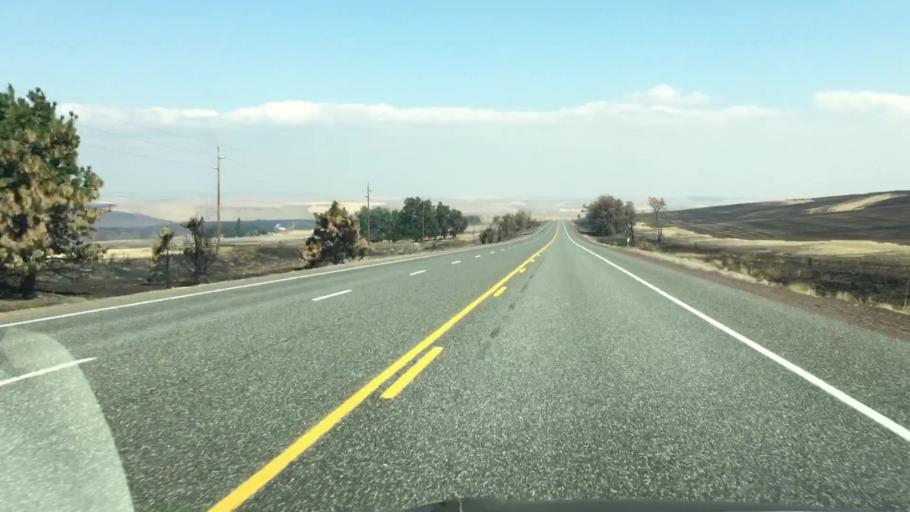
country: US
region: Oregon
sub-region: Wasco County
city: The Dalles
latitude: 45.3797
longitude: -121.1420
